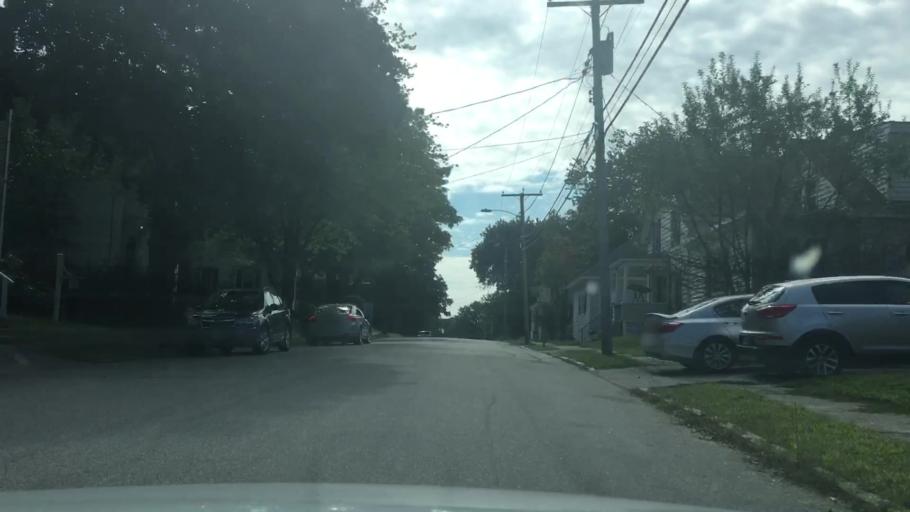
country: US
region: Maine
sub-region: Androscoggin County
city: Auburn
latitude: 44.0970
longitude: -70.2384
